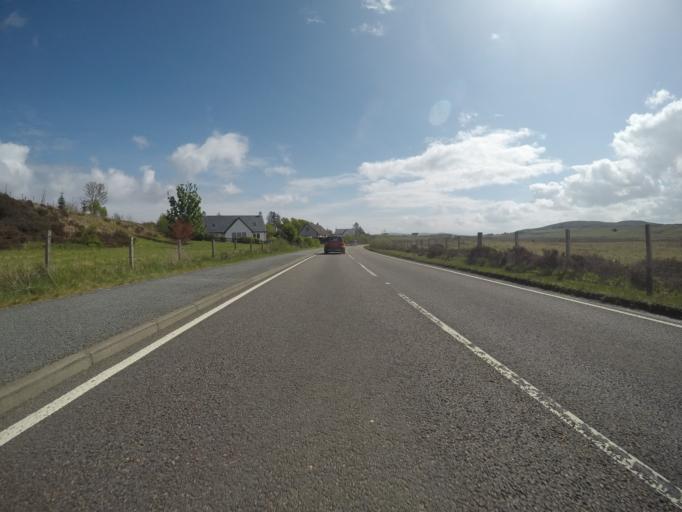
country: GB
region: Scotland
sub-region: Highland
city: Portree
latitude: 57.4814
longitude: -6.3020
